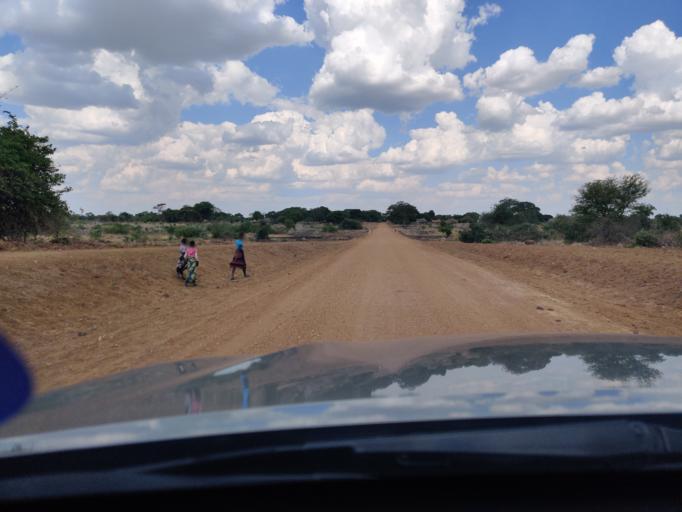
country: ZM
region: Central
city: Chibombo
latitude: -14.7617
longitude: 27.8917
